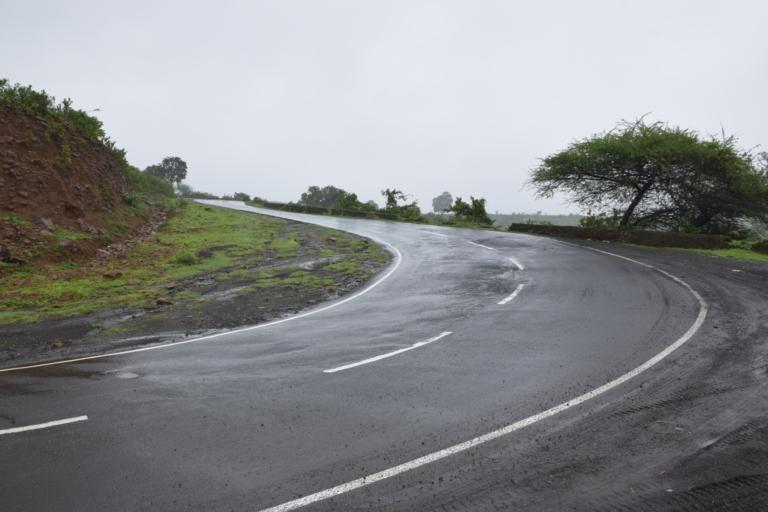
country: IN
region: Maharashtra
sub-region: Nashik Division
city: Surgana
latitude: 20.4772
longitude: 73.7503
